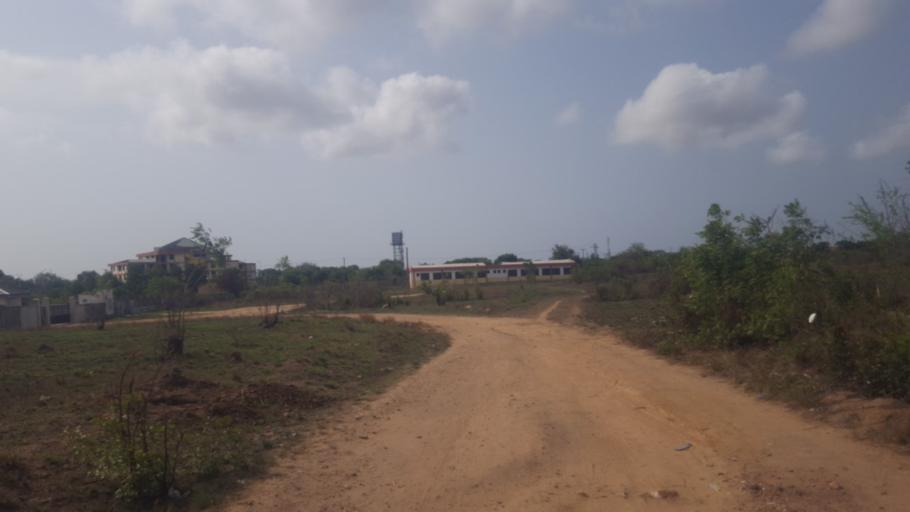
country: GH
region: Central
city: Winneba
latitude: 5.3768
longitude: -0.6427
